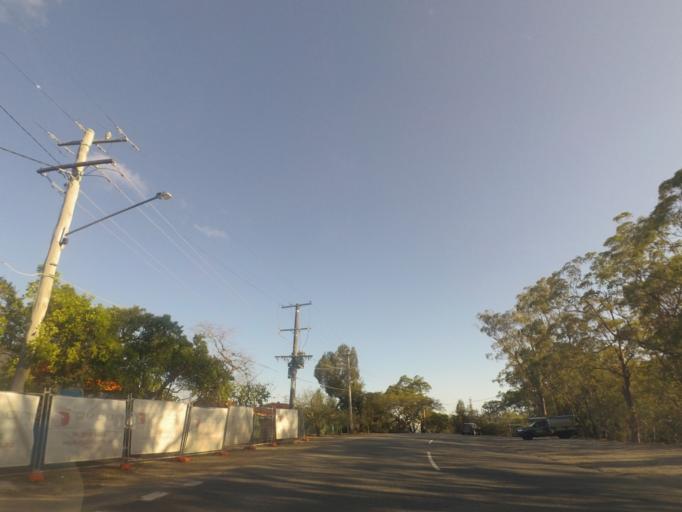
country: AU
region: Queensland
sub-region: Brisbane
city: Taringa
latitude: -27.4715
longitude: 152.9718
